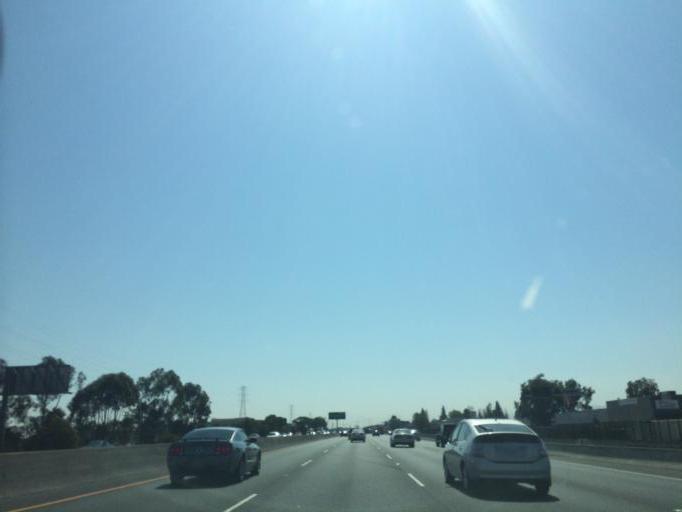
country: US
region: California
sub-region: San Mateo County
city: San Carlos
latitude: 37.5110
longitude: -122.2529
